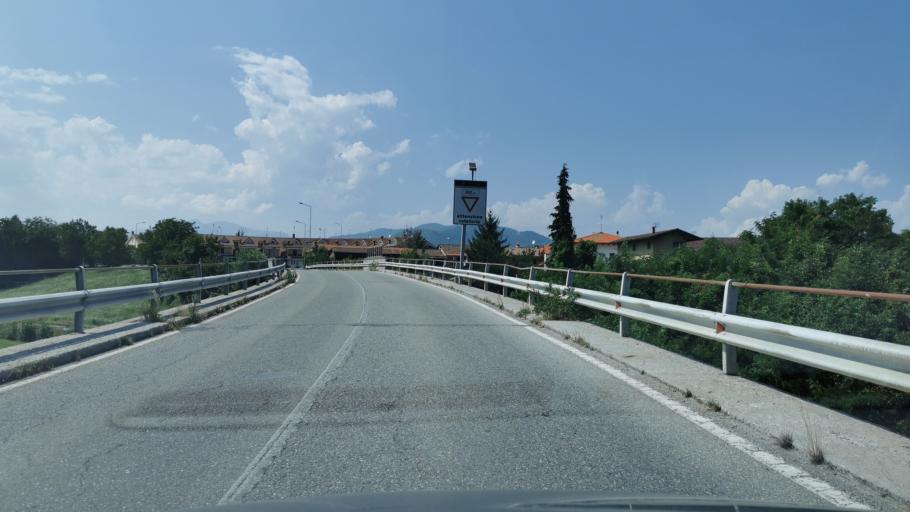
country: IT
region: Piedmont
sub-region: Provincia di Cuneo
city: Borgo San Dalmazzo
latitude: 44.3341
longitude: 7.5045
